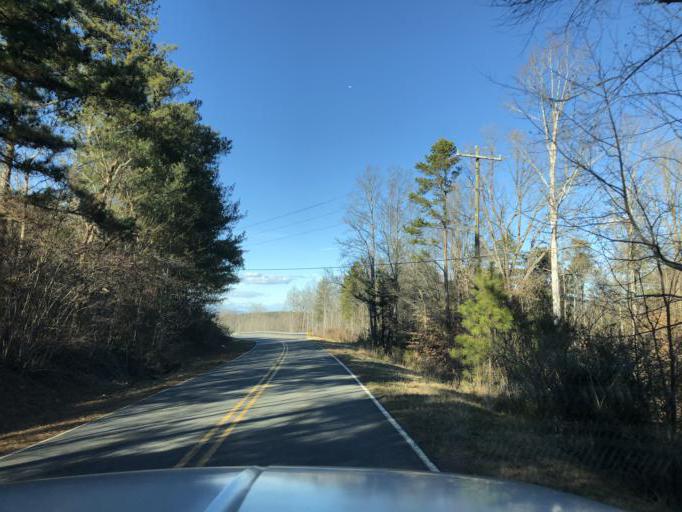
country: US
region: North Carolina
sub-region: Cleveland County
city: Shelby
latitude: 35.3223
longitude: -81.5384
